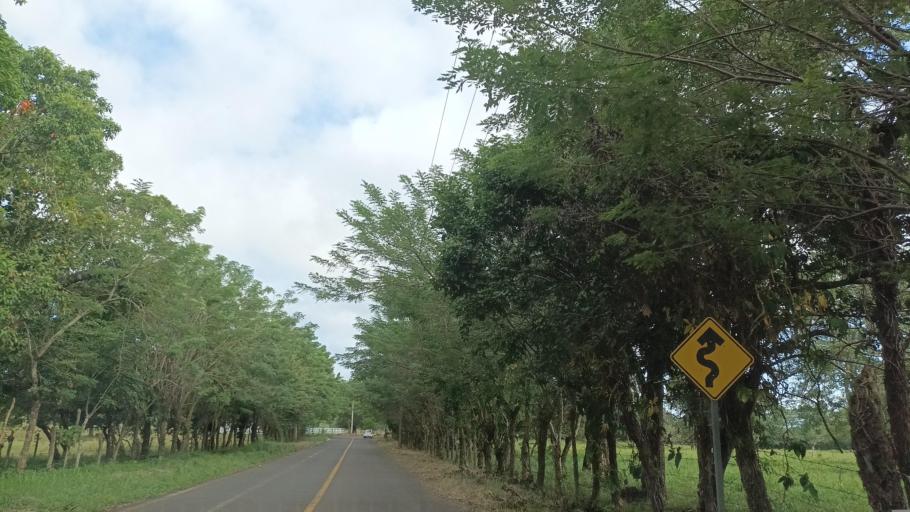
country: MX
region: Veracruz
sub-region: Pajapan
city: Pajapan
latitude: 18.1895
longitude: -94.6906
